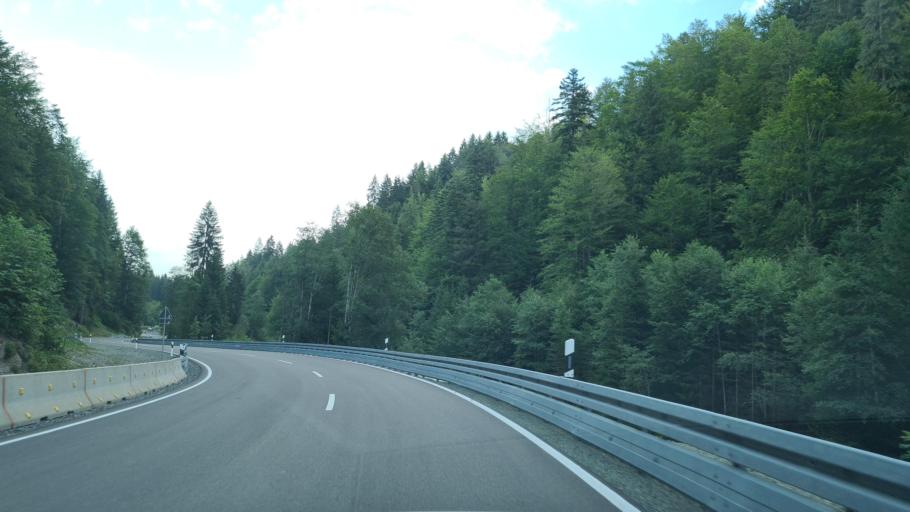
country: DE
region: Bavaria
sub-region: Swabia
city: Obermaiselstein
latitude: 47.4415
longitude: 10.2295
